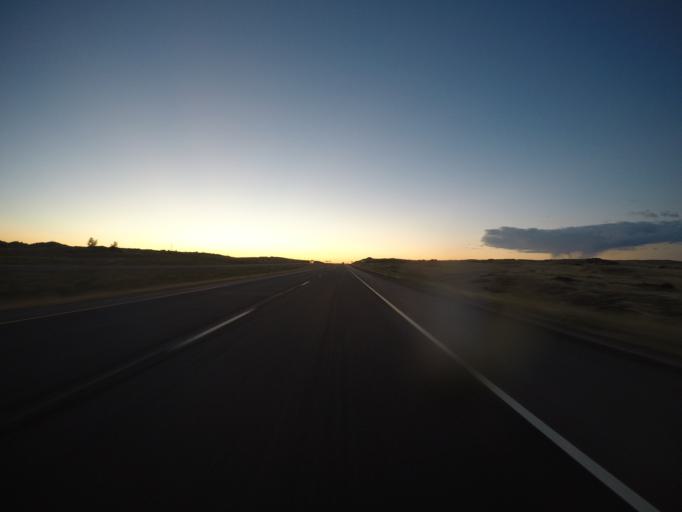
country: US
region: Wyoming
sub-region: Albany County
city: Laramie
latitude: 41.0483
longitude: -105.4647
